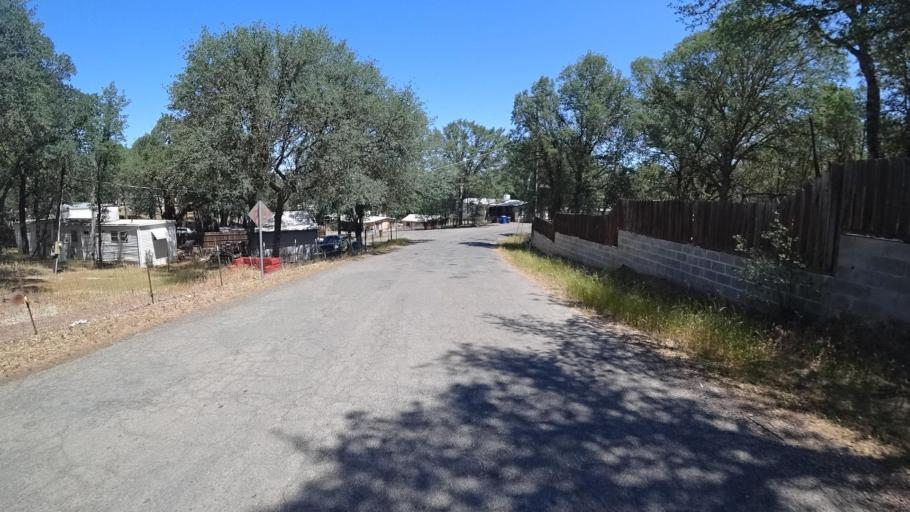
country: US
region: California
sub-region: Lake County
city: Lower Lake
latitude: 38.9142
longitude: -122.5989
